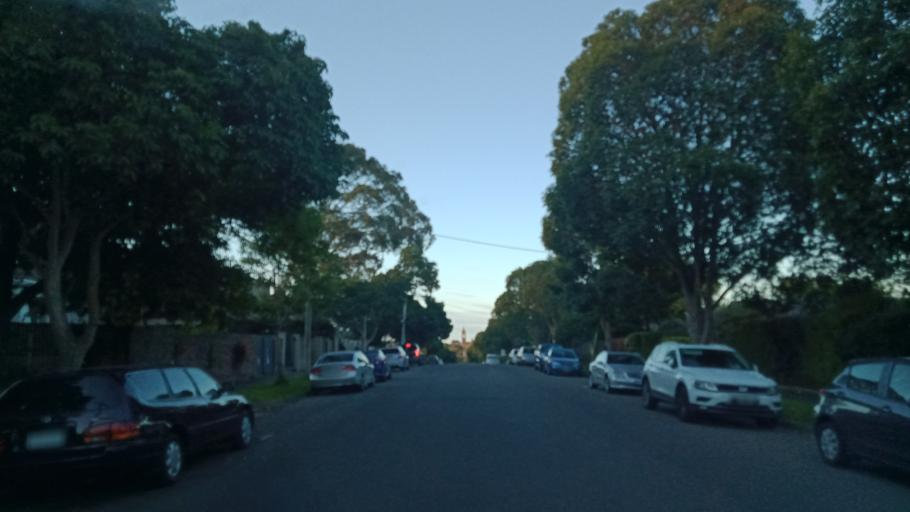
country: AU
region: Victoria
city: Glenferrie
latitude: -37.8331
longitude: 145.0411
